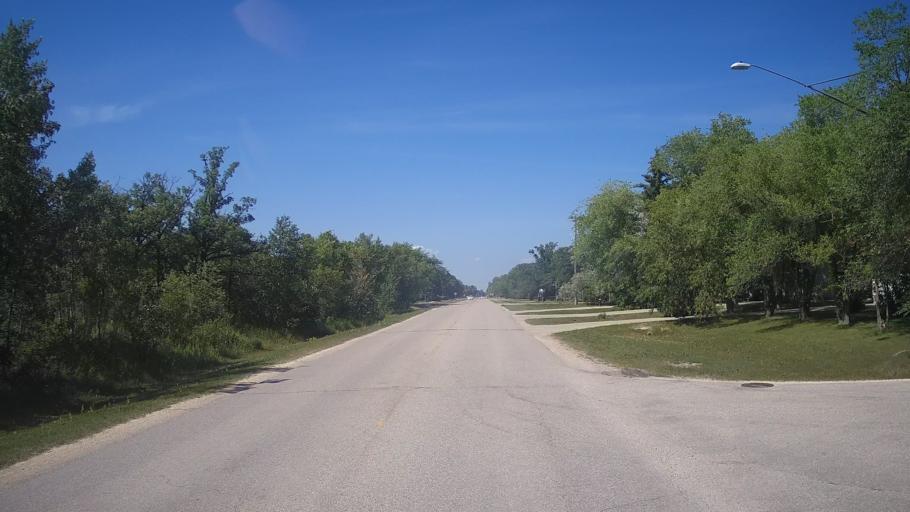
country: CA
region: Manitoba
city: Stonewall
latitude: 50.1249
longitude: -97.3333
